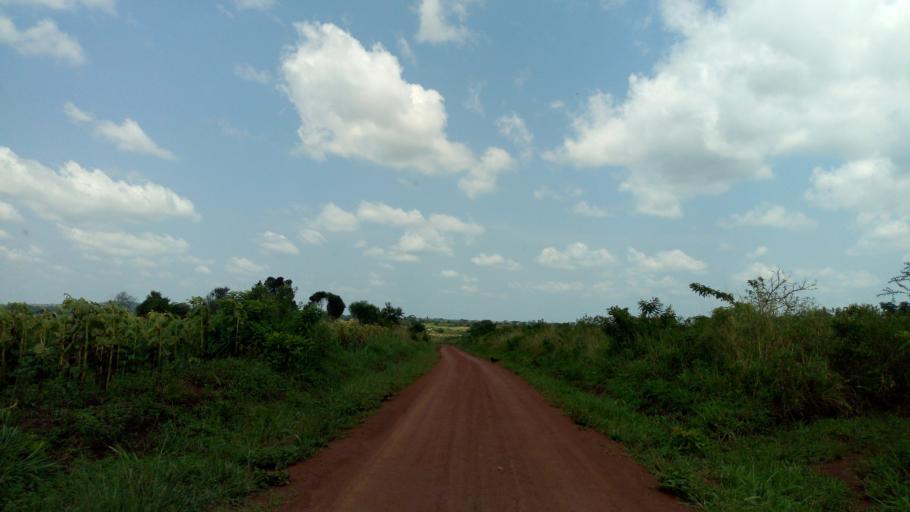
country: UG
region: Western Region
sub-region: Masindi District
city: Masindi
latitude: 1.7630
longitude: 31.8563
